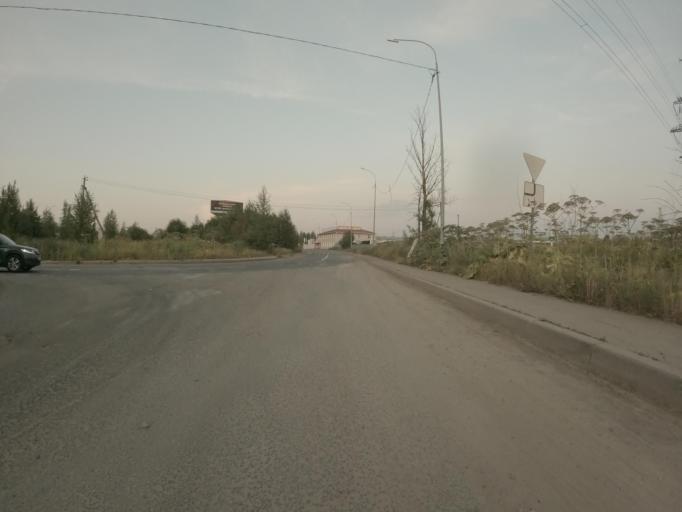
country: RU
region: St.-Petersburg
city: Krasnogvargeisky
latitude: 59.9448
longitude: 30.5113
